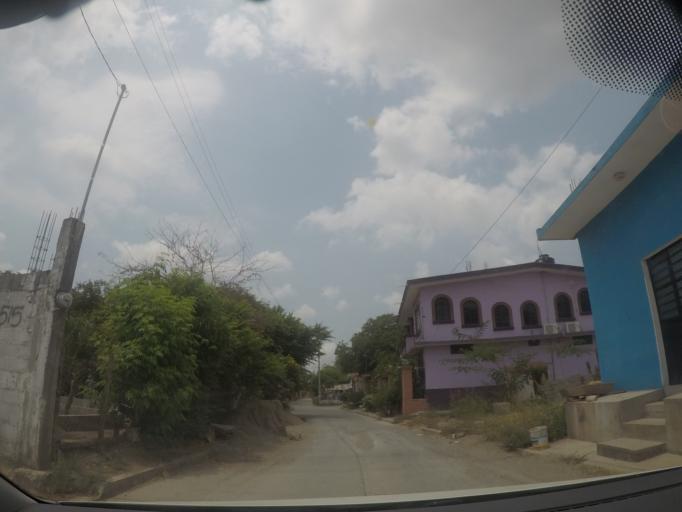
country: MX
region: Oaxaca
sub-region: El Espinal
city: El Espinal
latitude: 16.4896
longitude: -95.0461
